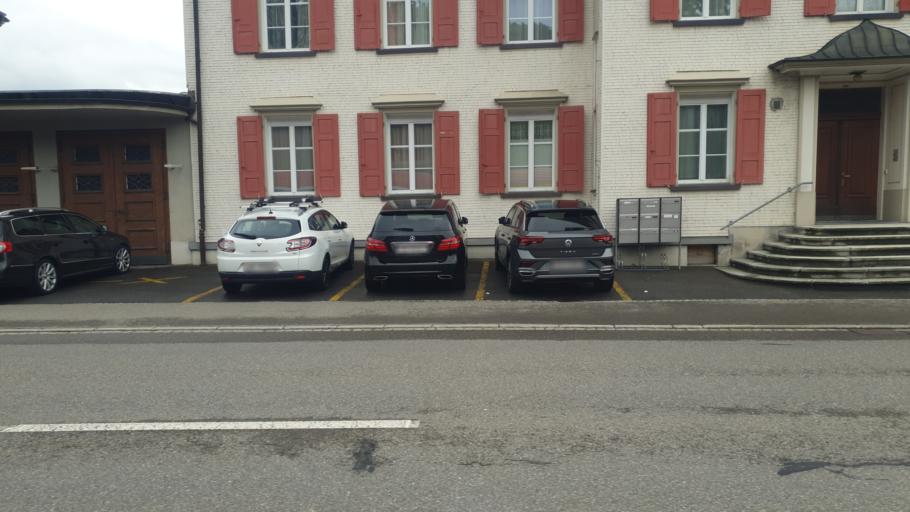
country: CH
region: Appenzell Ausserrhoden
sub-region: Bezirk Mittelland
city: Teufen
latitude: 47.3890
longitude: 9.3773
